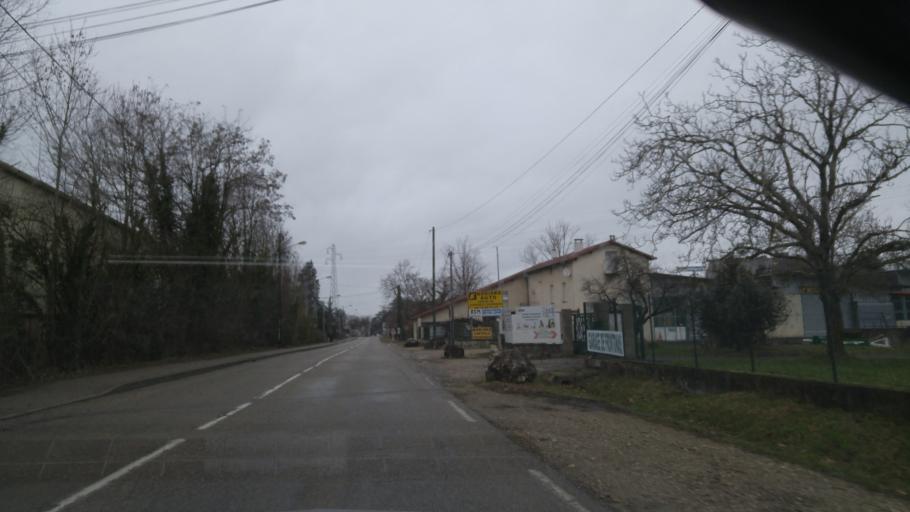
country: FR
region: Rhone-Alpes
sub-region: Departement de l'Isere
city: Villefontaine
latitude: 45.6252
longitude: 5.1534
